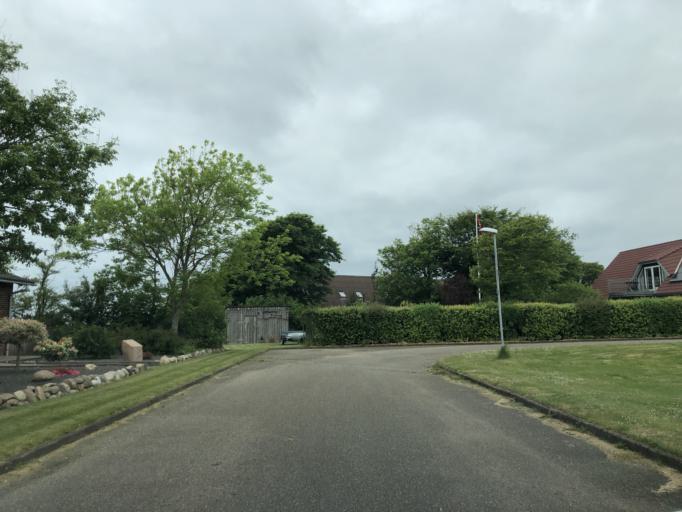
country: DK
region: Central Jutland
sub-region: Holstebro Kommune
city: Ulfborg
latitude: 56.2345
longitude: 8.1974
